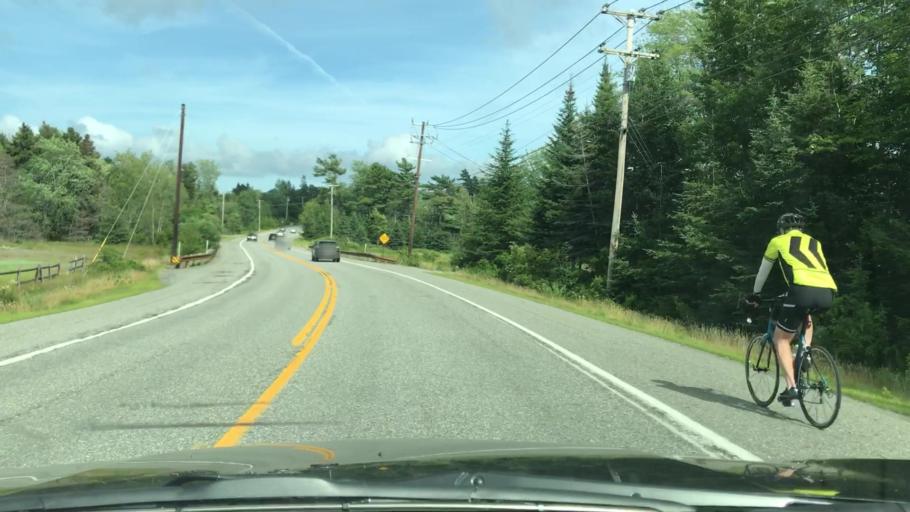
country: US
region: Maine
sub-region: Hancock County
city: Trenton
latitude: 44.4189
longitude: -68.3518
